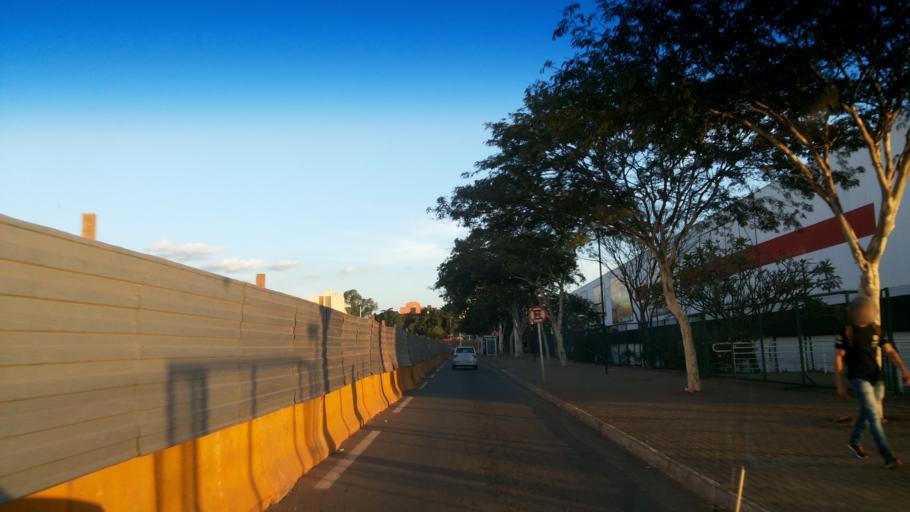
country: BR
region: Goias
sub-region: Goiania
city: Goiania
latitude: -16.6599
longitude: -49.2614
